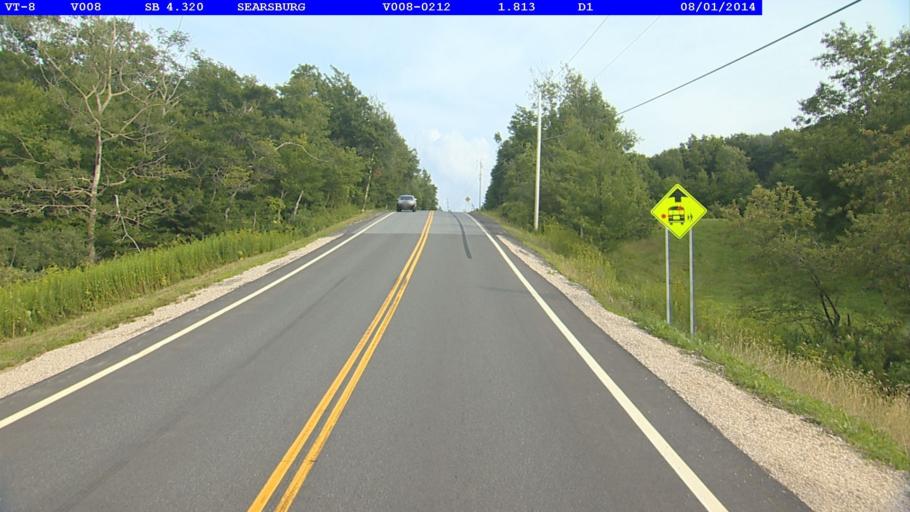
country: US
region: Vermont
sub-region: Windham County
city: Dover
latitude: 42.8828
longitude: -72.9725
